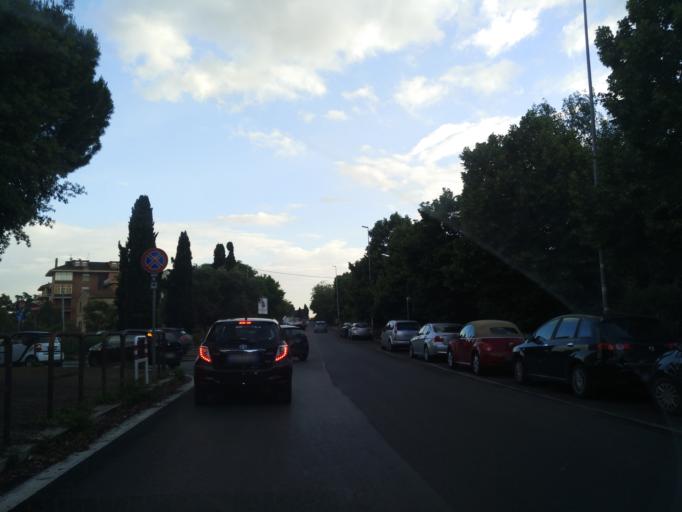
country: IT
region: Latium
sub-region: Citta metropolitana di Roma Capitale
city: Rome
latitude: 41.8804
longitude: 12.5600
